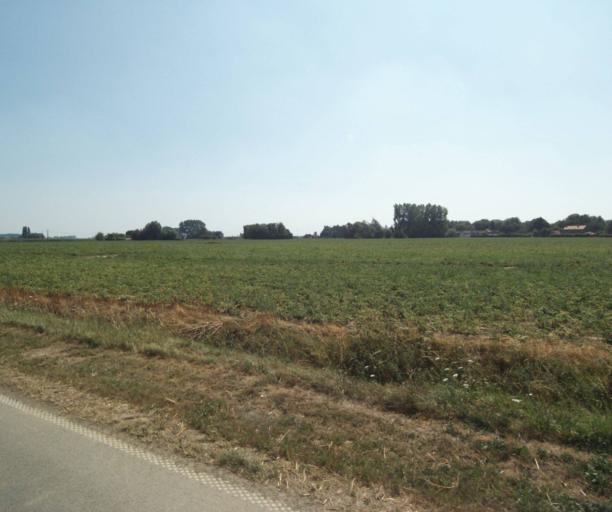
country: FR
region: Nord-Pas-de-Calais
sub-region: Departement du Nord
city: Comines
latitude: 50.7511
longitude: 3.0331
